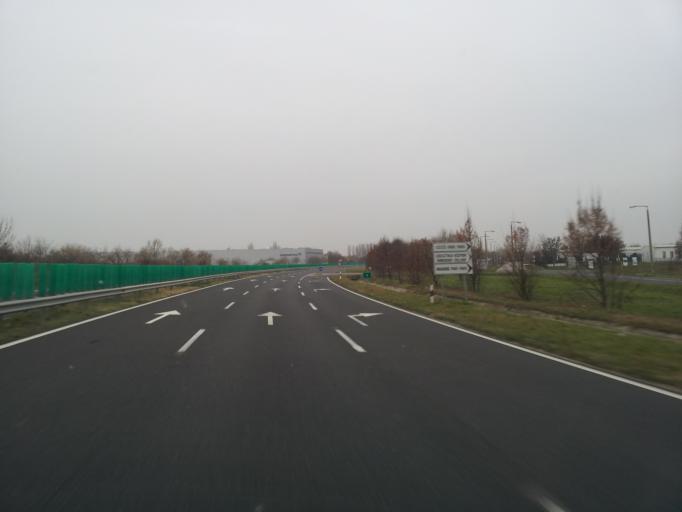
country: HU
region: Fejer
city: Szekesfehervar
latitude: 47.1485
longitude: 18.4216
